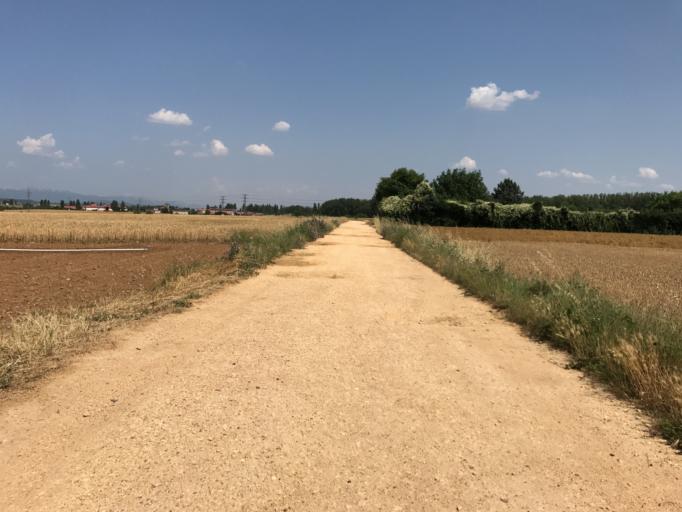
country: ES
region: Basque Country
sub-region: Provincia de Alava
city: Gasteiz / Vitoria
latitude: 42.8773
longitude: -2.6710
